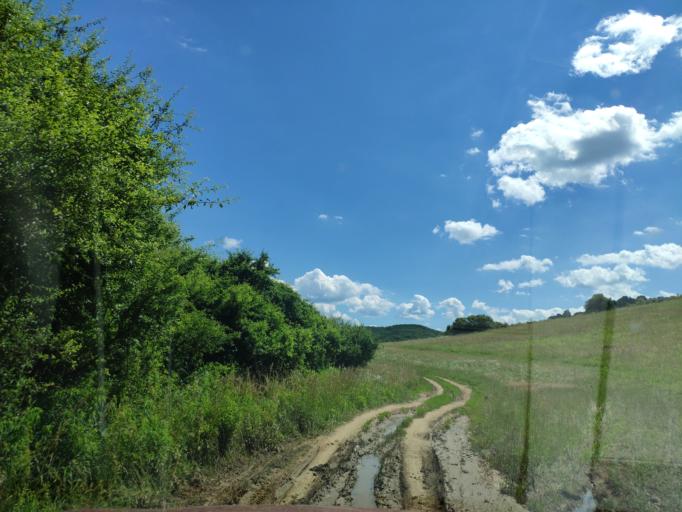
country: HU
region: Borsod-Abauj-Zemplen
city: Arlo
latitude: 48.2670
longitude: 20.1969
